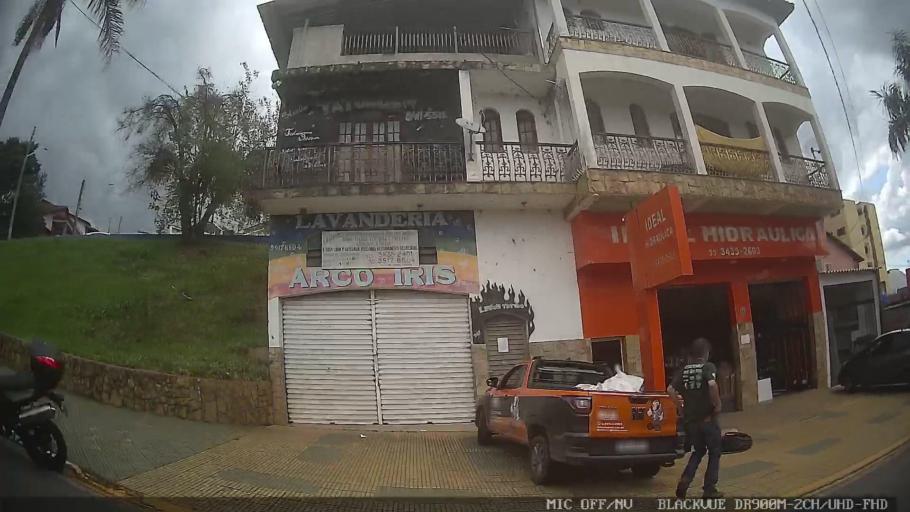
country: BR
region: Minas Gerais
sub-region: Extrema
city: Extrema
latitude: -22.8514
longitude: -46.3189
